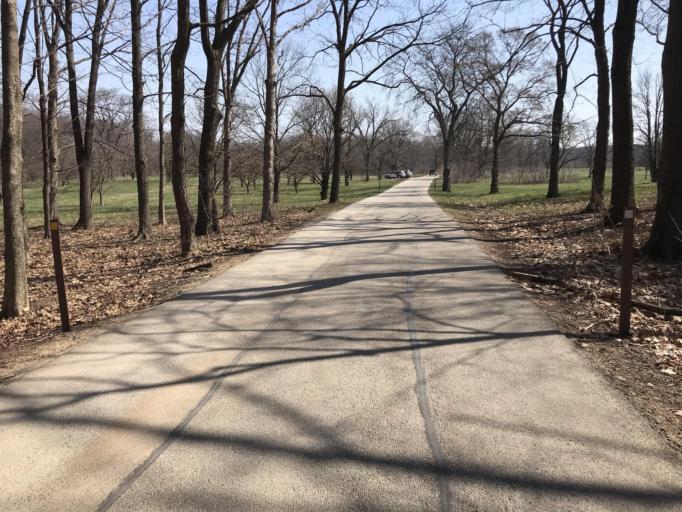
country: US
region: Illinois
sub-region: DuPage County
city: Lisle
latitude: 41.8147
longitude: -88.0572
